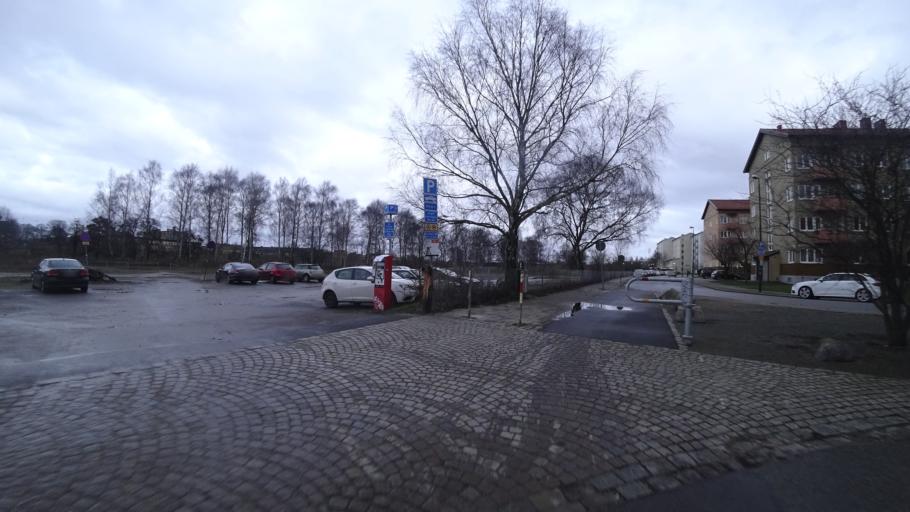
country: SE
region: Skane
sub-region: Malmo
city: Malmoe
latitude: 55.6056
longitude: 13.0312
